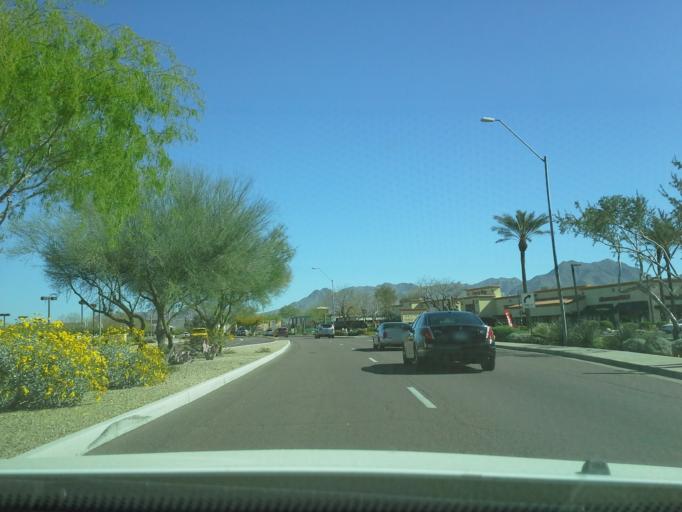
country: US
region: Arizona
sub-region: Maricopa County
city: Paradise Valley
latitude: 33.6279
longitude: -111.8947
